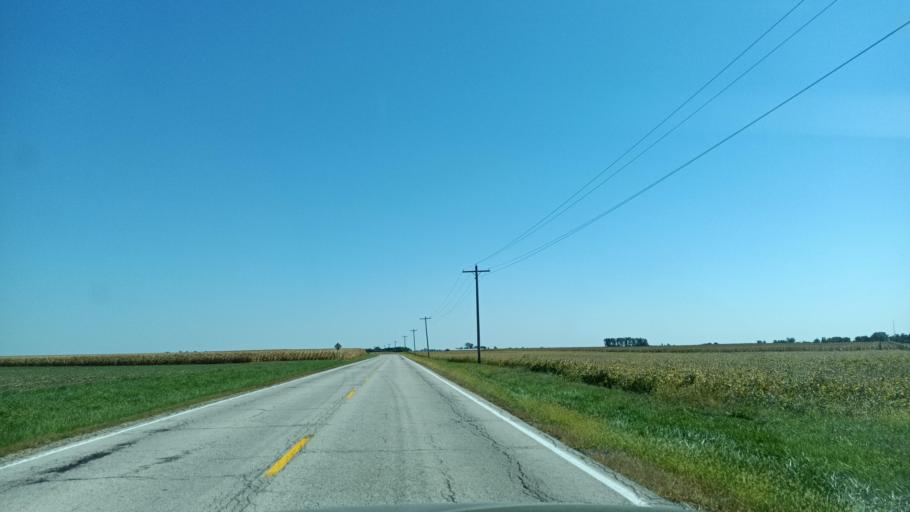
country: US
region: Illinois
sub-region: McLean County
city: Le Roy
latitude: 40.3086
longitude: -88.6980
